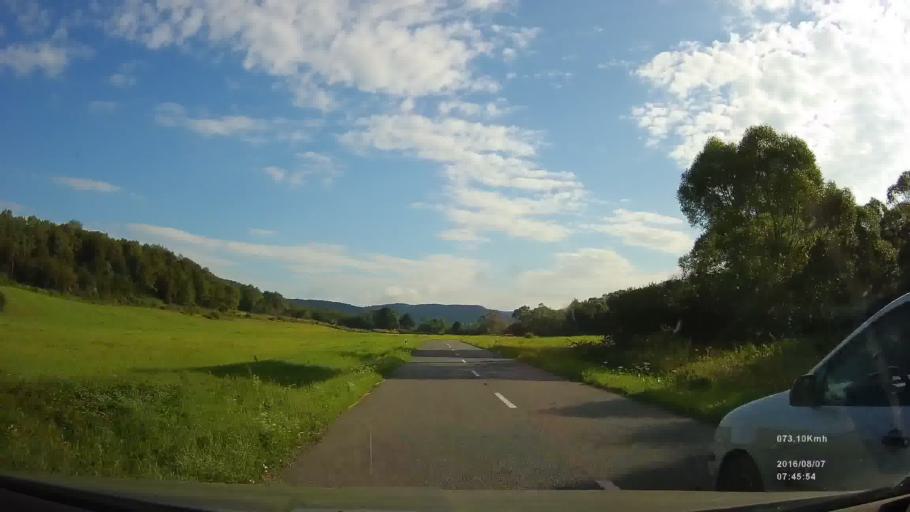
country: SK
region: Presovsky
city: Stropkov
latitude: 49.2633
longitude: 21.7462
